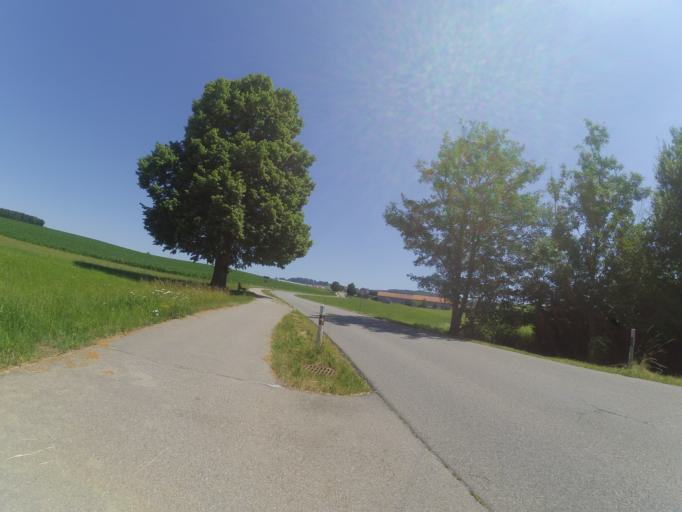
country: DE
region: Bavaria
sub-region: Swabia
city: Haldenwang
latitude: 47.7931
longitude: 10.3259
